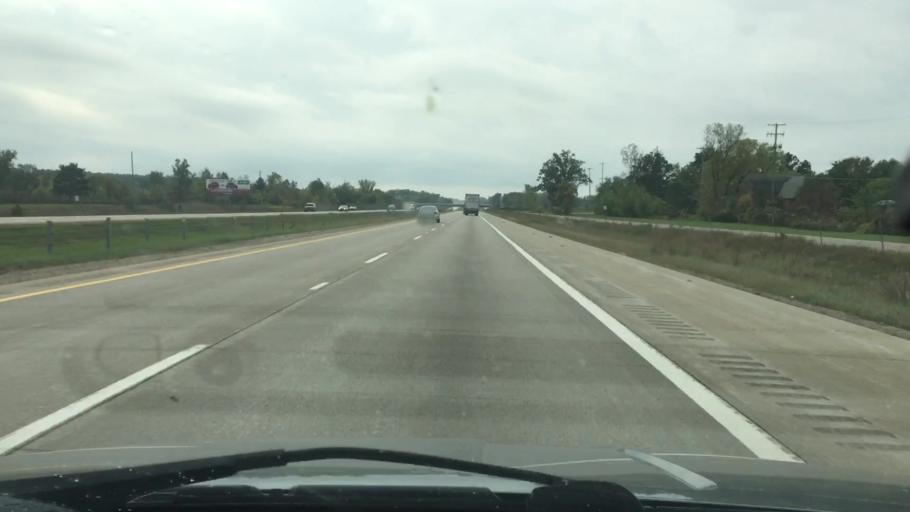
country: US
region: Michigan
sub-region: Genesee County
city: Fenton
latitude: 42.7140
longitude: -83.7627
